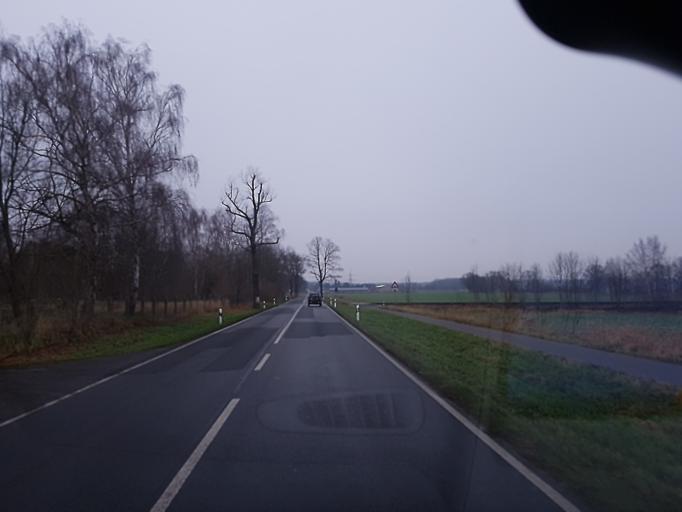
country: DE
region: Brandenburg
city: Lubbenau
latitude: 51.8756
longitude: 13.9116
